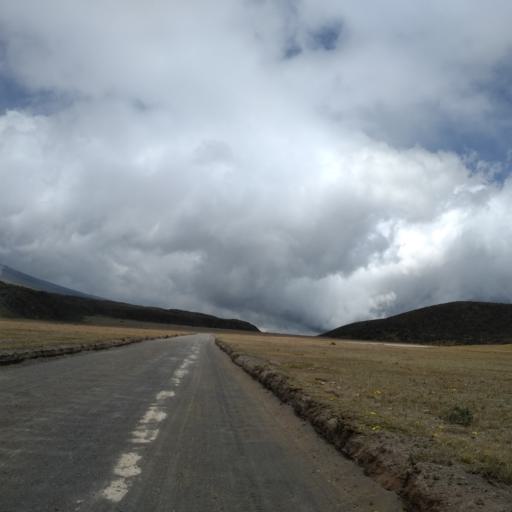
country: EC
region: Pichincha
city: Machachi
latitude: -0.6168
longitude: -78.4737
